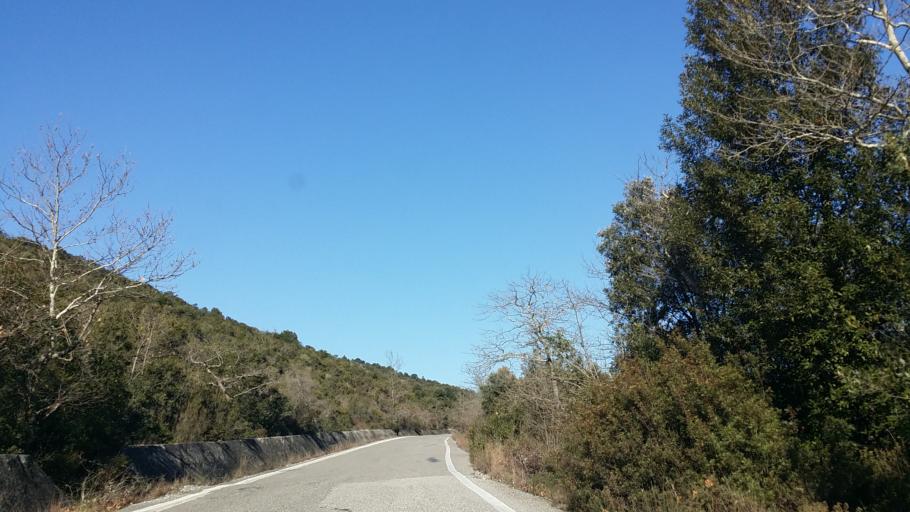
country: GR
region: West Greece
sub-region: Nomos Aitolias kai Akarnanias
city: Lepenou
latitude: 38.7802
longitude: 21.3351
